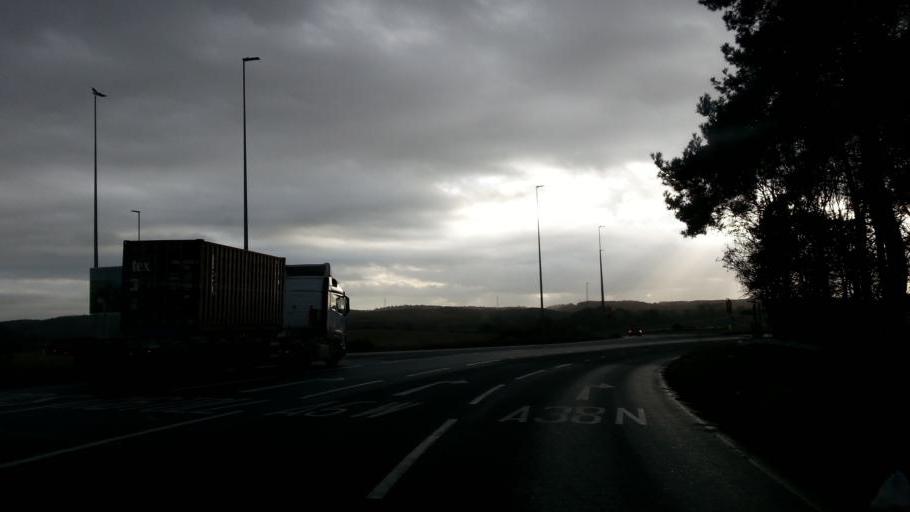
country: GB
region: England
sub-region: Staffordshire
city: Shenstone
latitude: 52.6397
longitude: -1.8032
